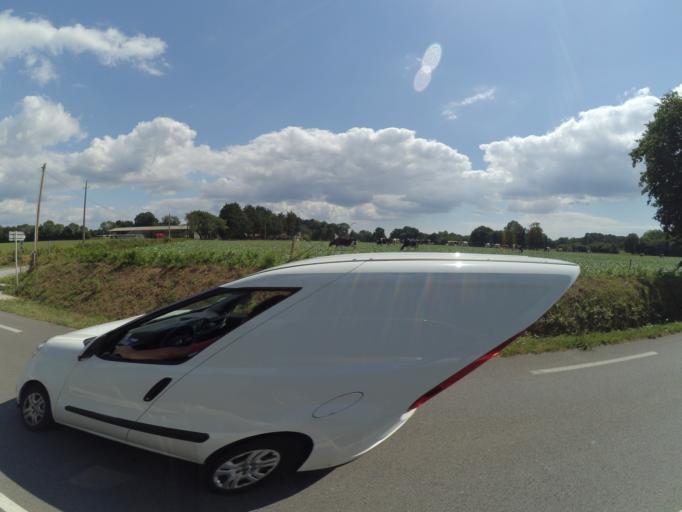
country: FR
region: Brittany
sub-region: Departement du Morbihan
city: Nostang
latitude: 47.7518
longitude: -3.1578
